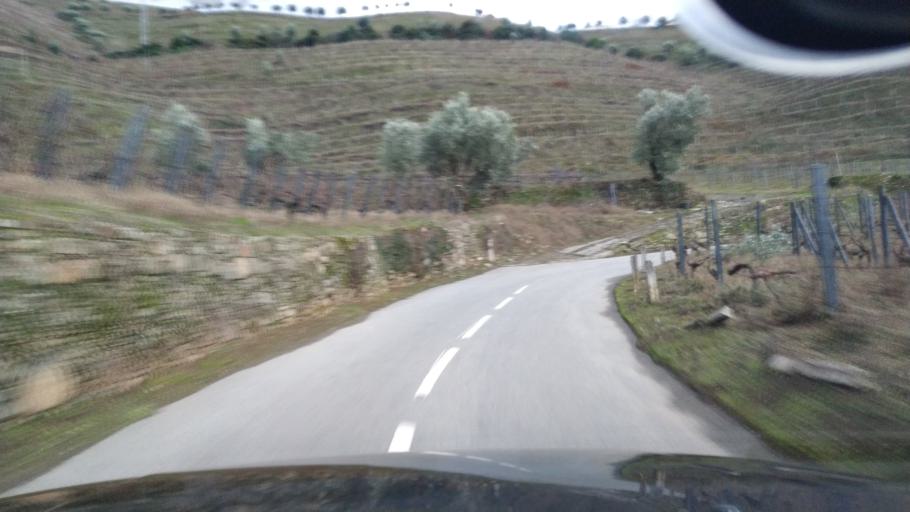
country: PT
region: Vila Real
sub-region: Santa Marta de Penaguiao
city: Santa Marta de Penaguiao
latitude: 41.2411
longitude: -7.7766
